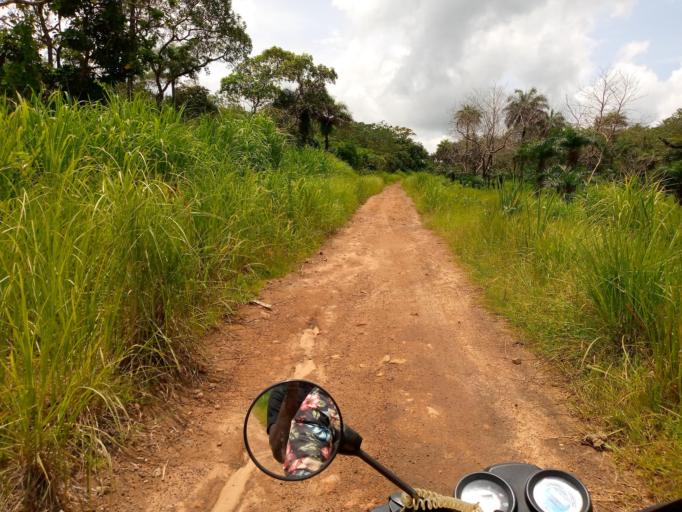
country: SL
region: Northern Province
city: Binkolo
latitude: 9.1206
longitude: -12.1336
